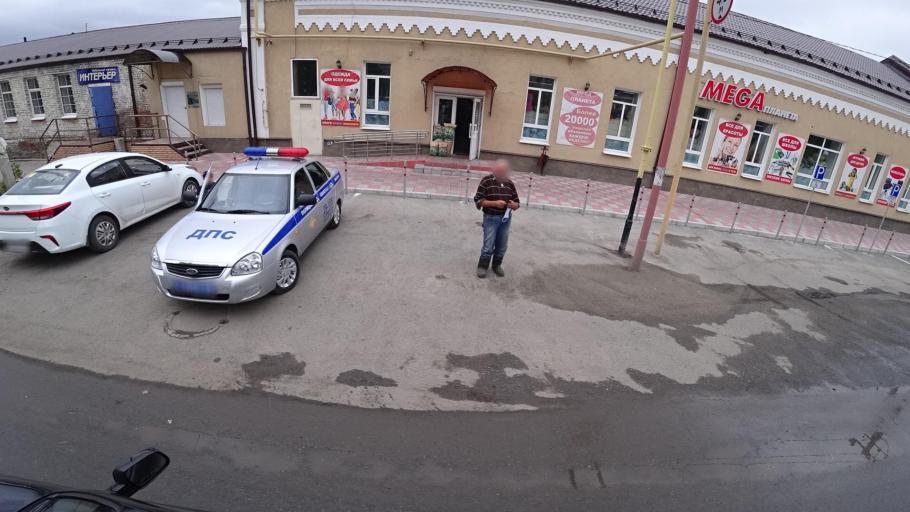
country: RU
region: Sverdlovsk
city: Kamyshlov
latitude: 56.8452
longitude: 62.7147
